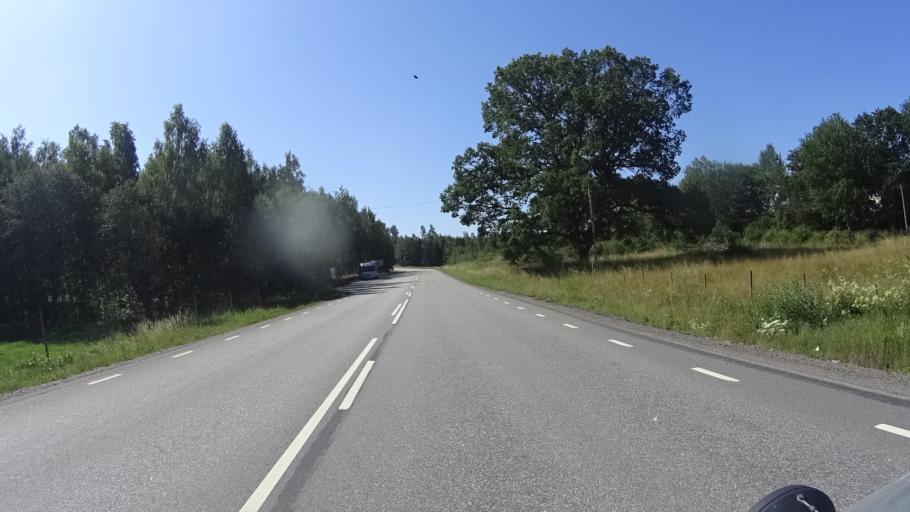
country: SE
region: OEstergoetland
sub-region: Vadstena Kommun
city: Herrestad
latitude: 58.3023
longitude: 14.9207
